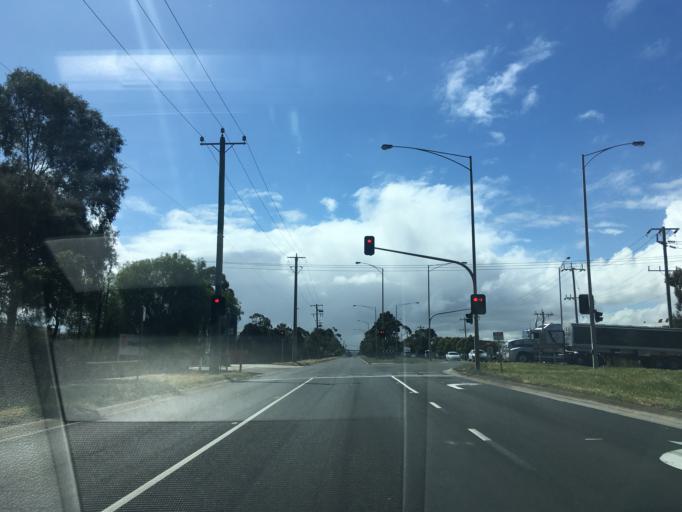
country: AU
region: Victoria
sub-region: Brimbank
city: Derrimut
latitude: -37.8212
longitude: 144.7863
